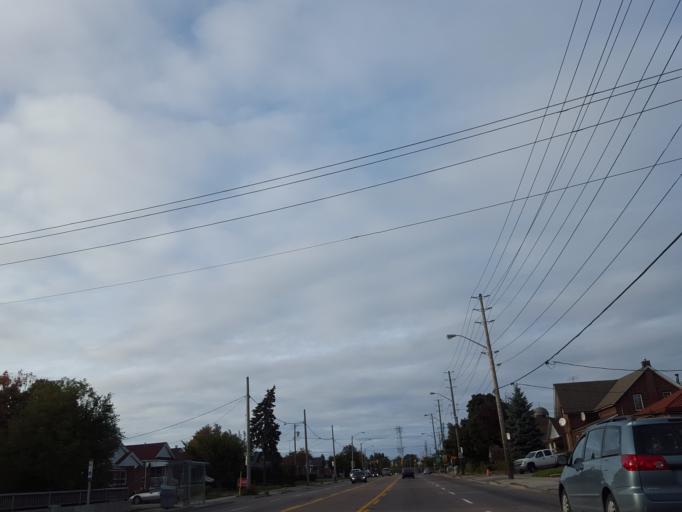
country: CA
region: Ontario
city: Scarborough
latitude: 43.7560
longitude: -79.2990
